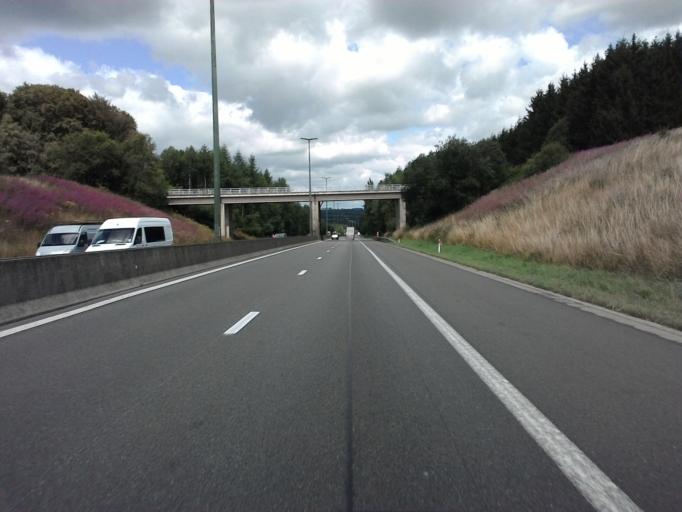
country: BE
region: Wallonia
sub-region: Province du Luxembourg
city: Leglise
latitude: 49.7841
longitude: 5.5353
